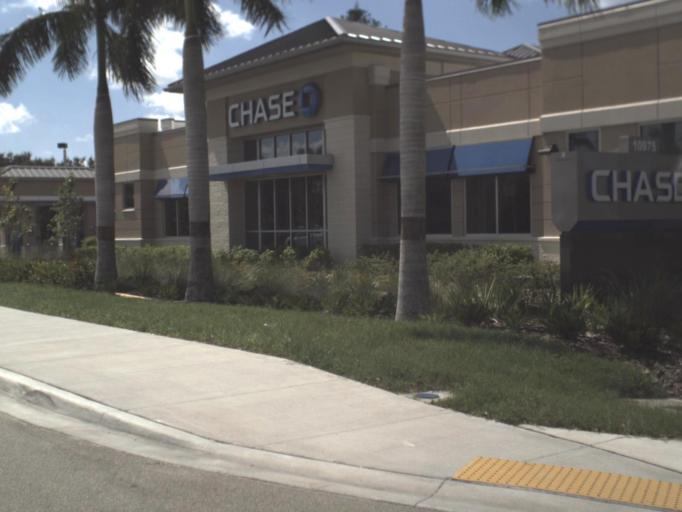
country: US
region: Florida
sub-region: Collier County
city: Naples Park
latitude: 26.2716
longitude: -81.8017
